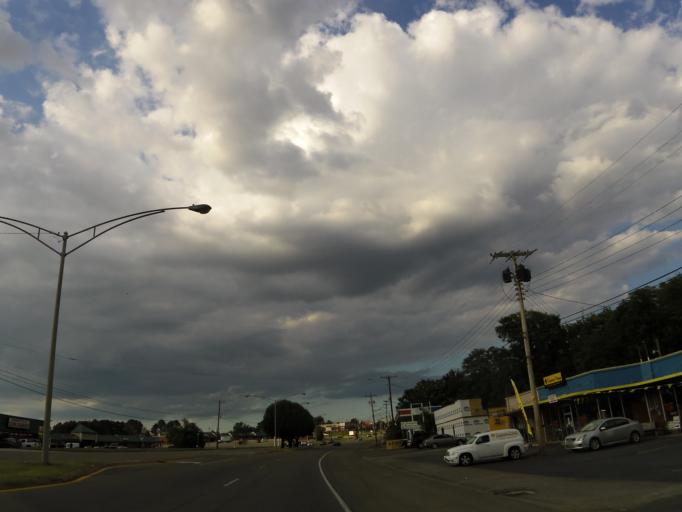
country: US
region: Tennessee
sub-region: Maury County
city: Columbia
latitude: 35.6248
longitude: -87.0324
